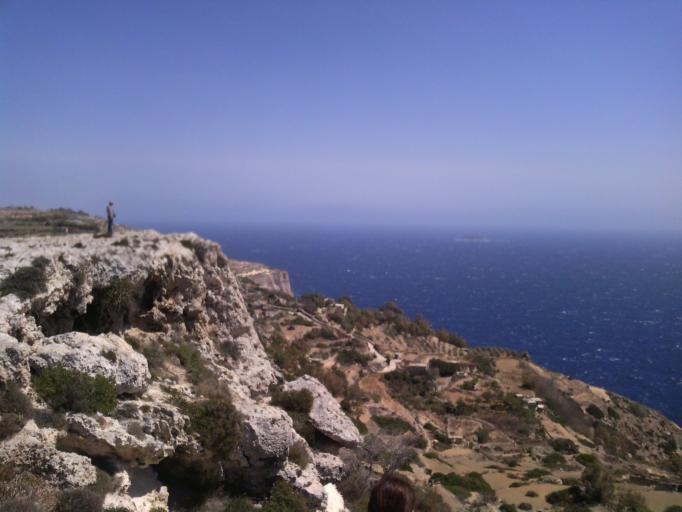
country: MT
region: Dingli
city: Dingli
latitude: 35.8517
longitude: 14.3858
